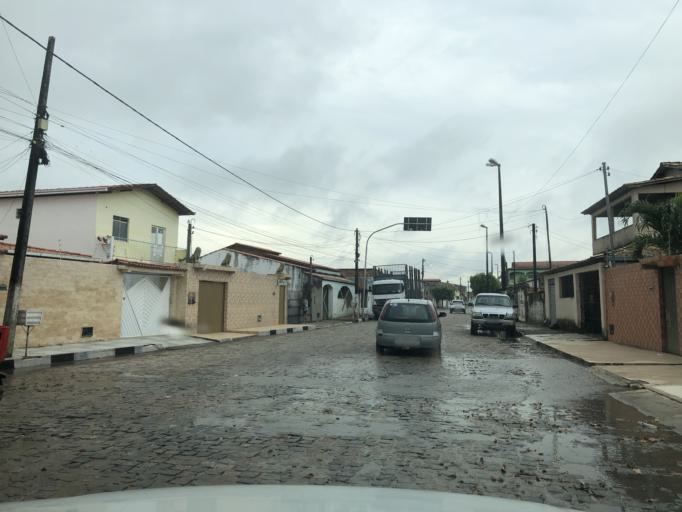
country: BR
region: Bahia
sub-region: Esplanada
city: Esplanada
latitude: -11.7947
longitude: -37.9525
